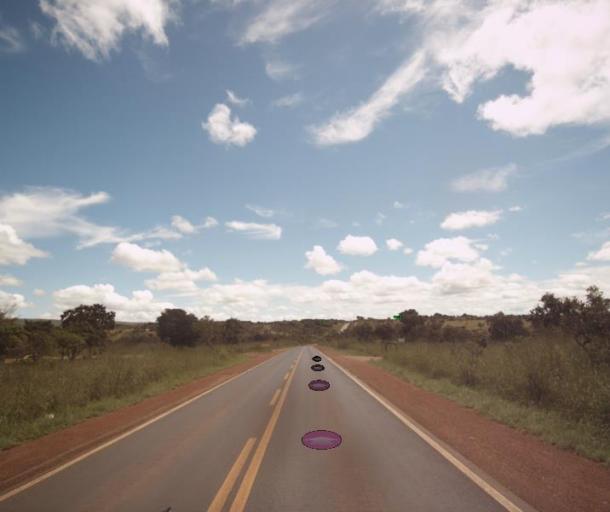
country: BR
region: Goias
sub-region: Padre Bernardo
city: Padre Bernardo
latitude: -15.3747
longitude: -48.2165
